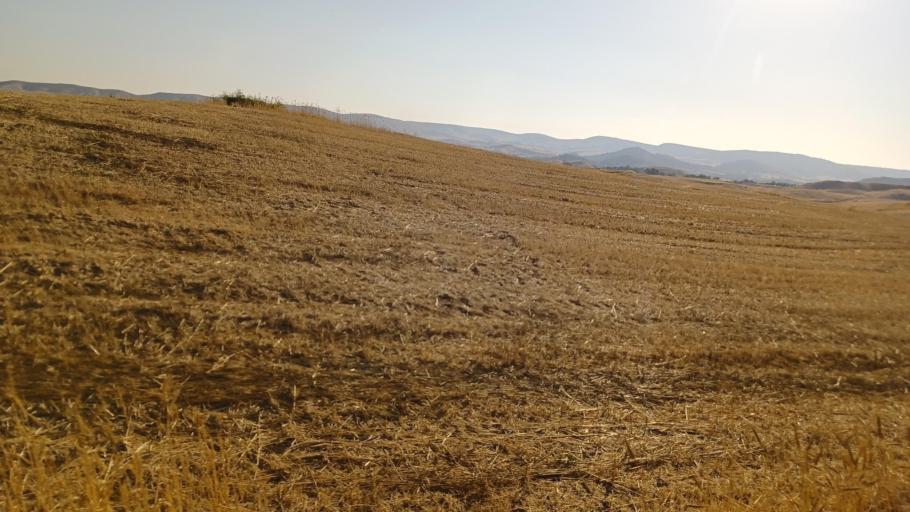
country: CY
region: Larnaka
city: Troulloi
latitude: 35.0087
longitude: 33.6090
